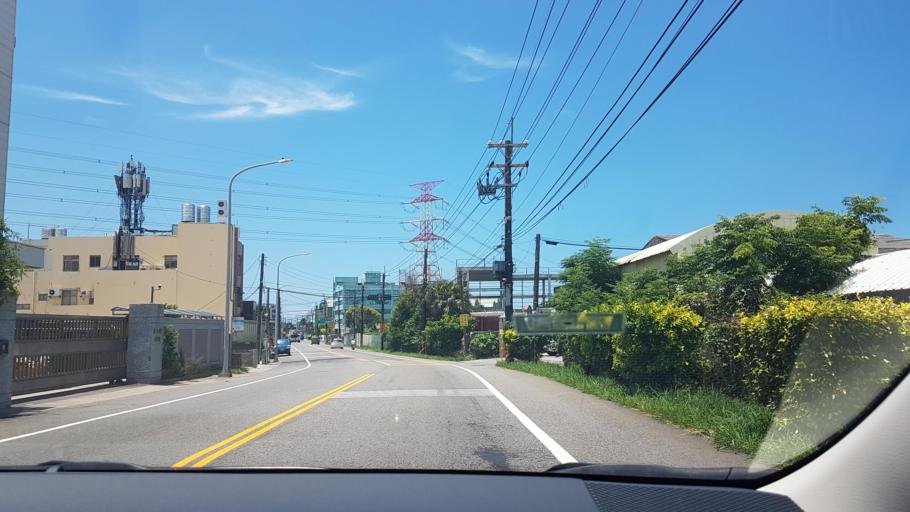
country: TW
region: Taiwan
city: Taoyuan City
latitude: 25.0900
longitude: 121.2762
